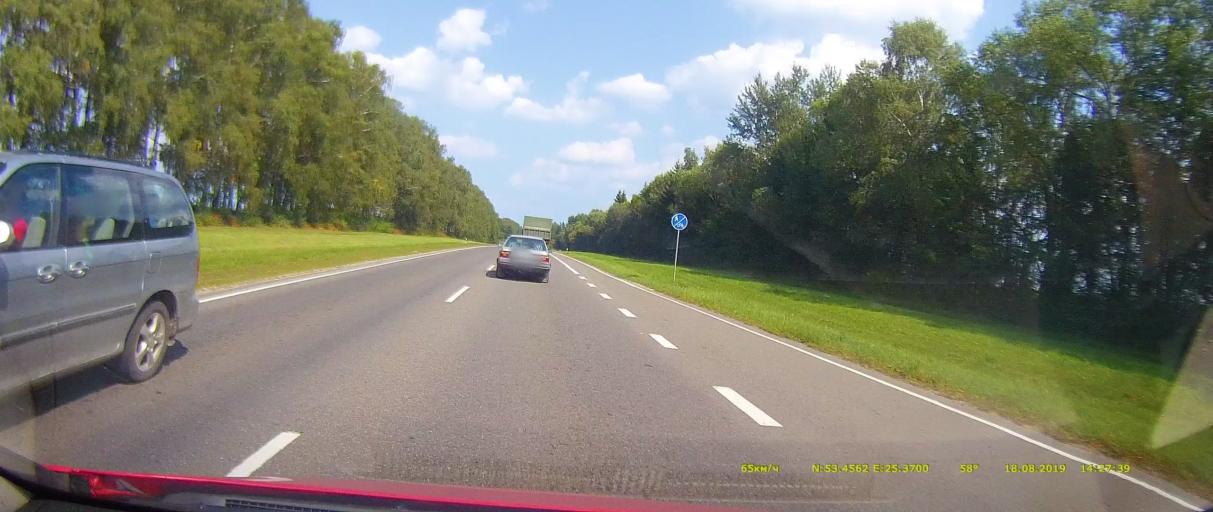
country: BY
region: Grodnenskaya
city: Dzyatlava
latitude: 53.4622
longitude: 25.3856
